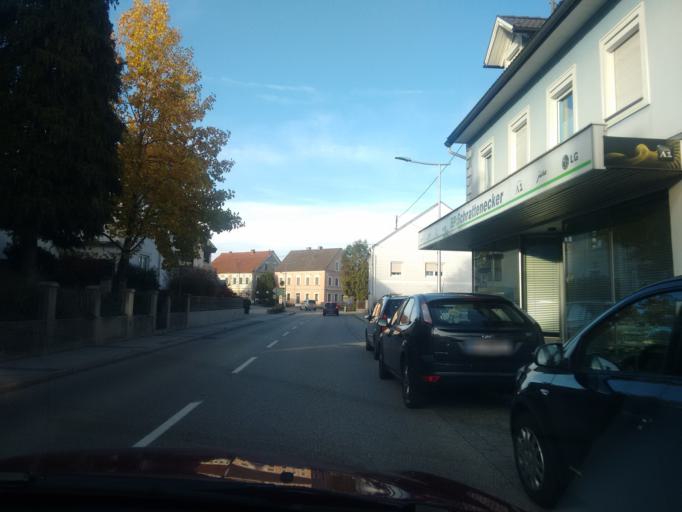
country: AT
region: Upper Austria
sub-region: Politischer Bezirk Vocklabruck
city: Niederthalheim
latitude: 48.1410
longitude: 13.7366
